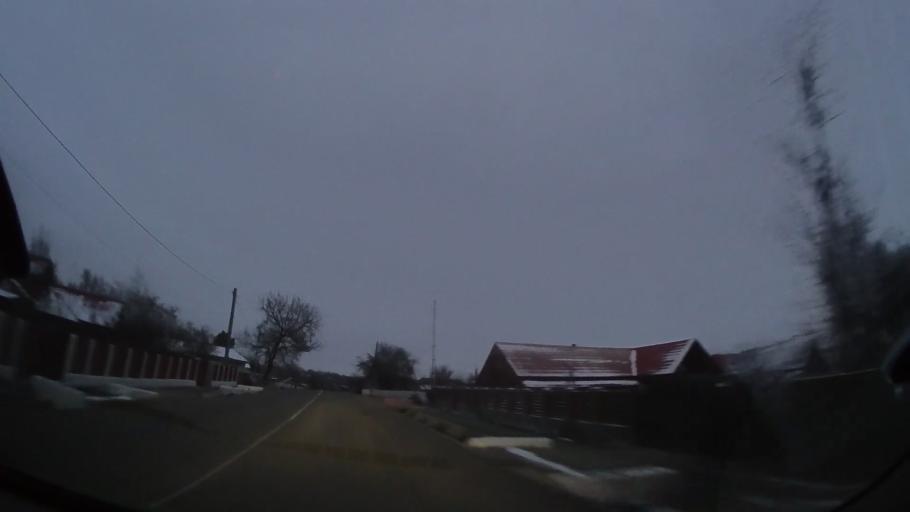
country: RO
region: Vaslui
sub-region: Comuna Vutcani
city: Vutcani
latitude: 46.4518
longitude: 28.0199
